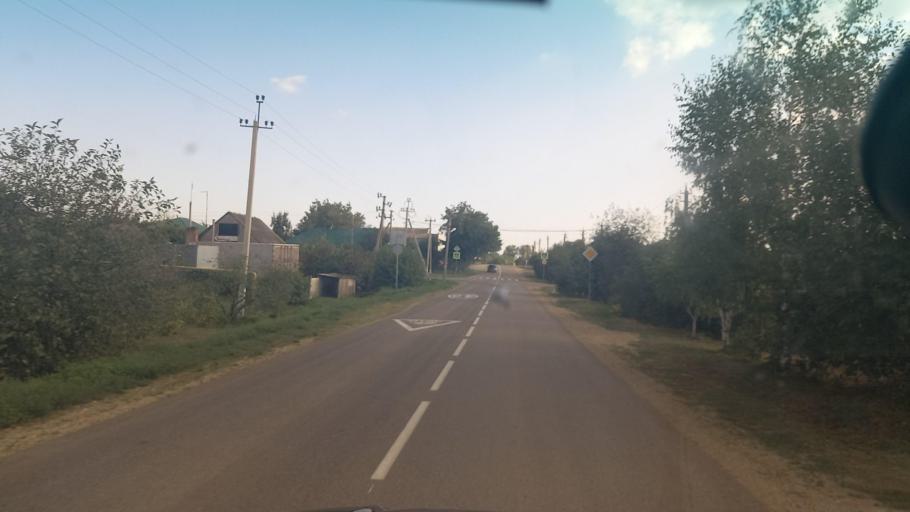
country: RU
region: Adygeya
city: Khatukay
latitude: 45.2967
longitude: 39.5574
